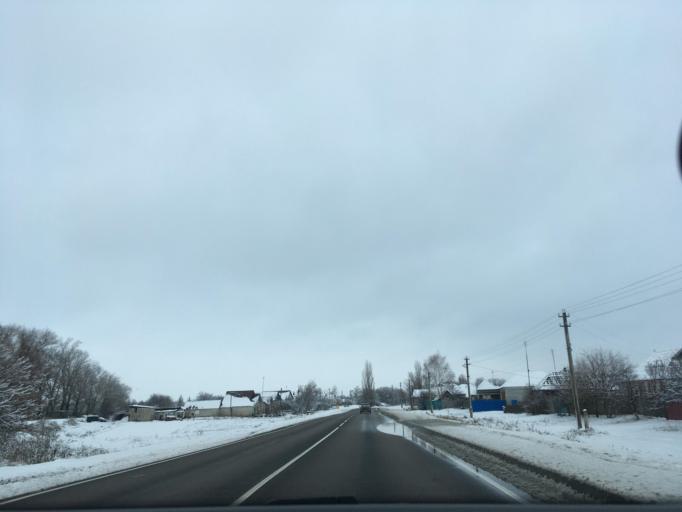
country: RU
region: Voronezj
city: Zabolotovka
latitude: 50.2475
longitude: 39.3593
